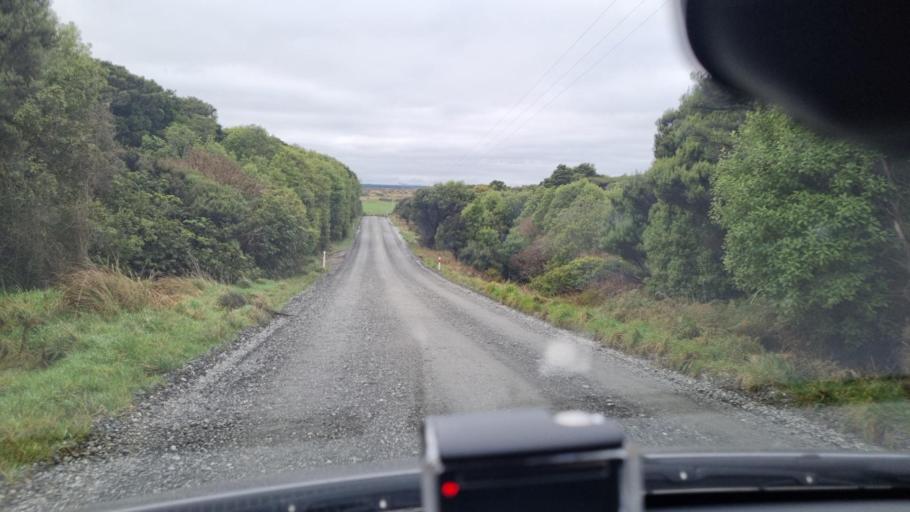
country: NZ
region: Southland
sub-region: Invercargill City
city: Bluff
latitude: -46.5246
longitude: 168.2707
